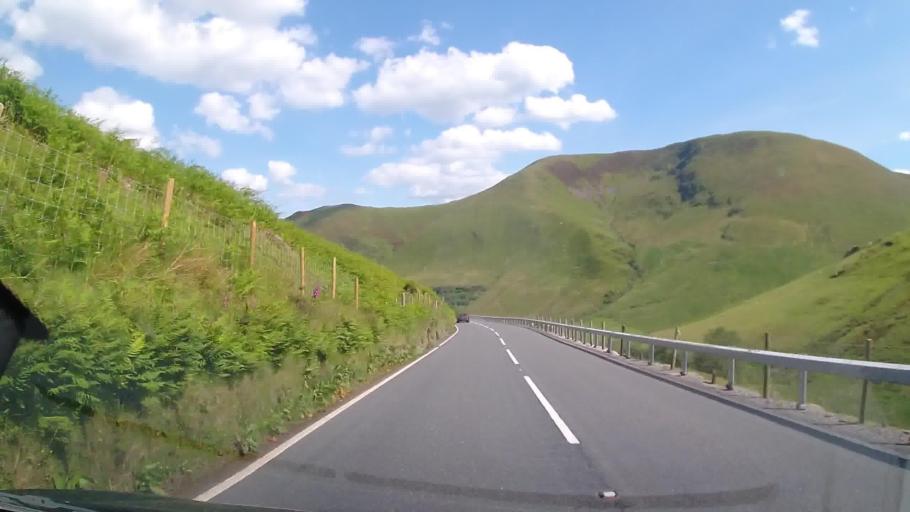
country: GB
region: Wales
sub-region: Gwynedd
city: Corris
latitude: 52.7339
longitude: -3.7627
